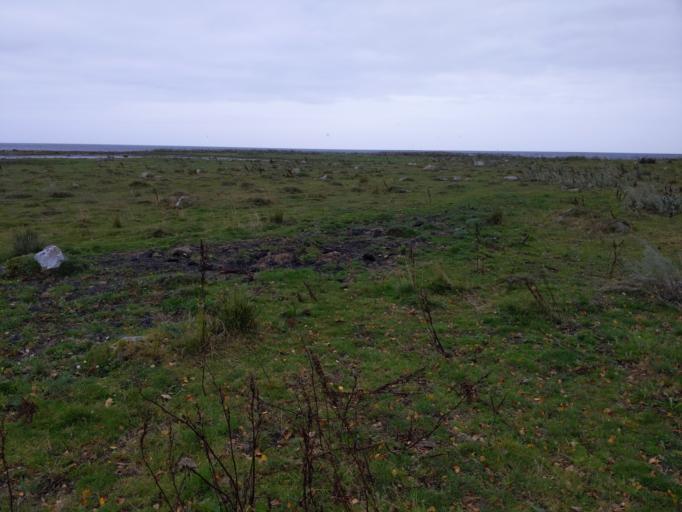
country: SE
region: Blekinge
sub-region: Karlskrona Kommun
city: Jaemjoe
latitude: 56.1976
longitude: 15.9668
